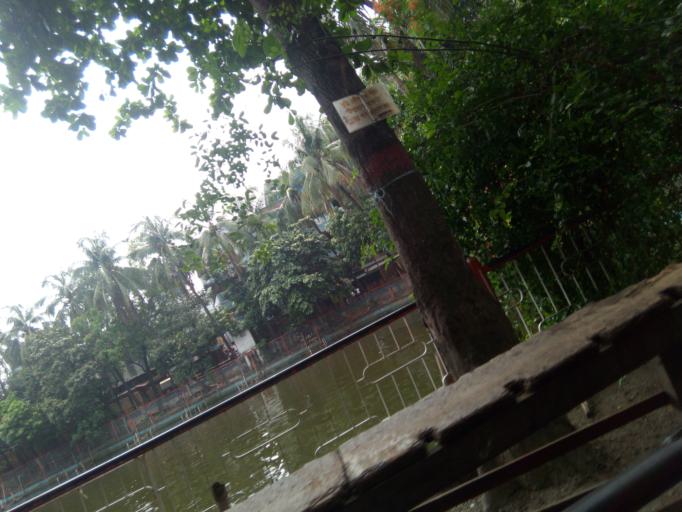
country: BD
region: Dhaka
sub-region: Dhaka
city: Dhaka
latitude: 23.7159
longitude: 90.4075
